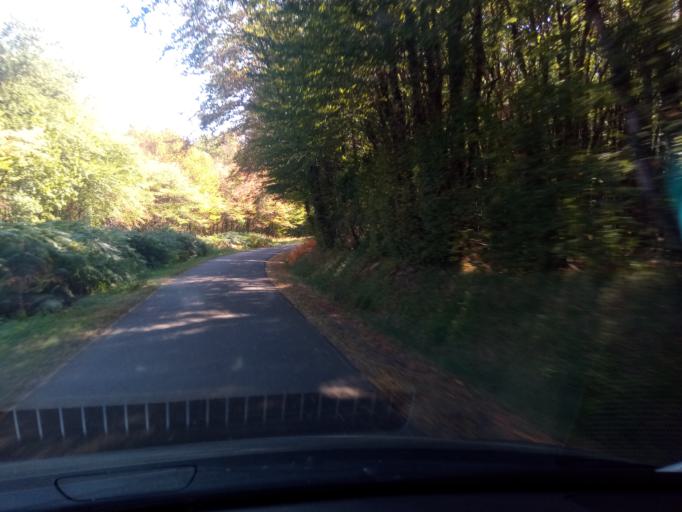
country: FR
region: Poitou-Charentes
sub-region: Departement de la Vienne
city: Lussac-les-Chateaux
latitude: 46.3846
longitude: 0.7699
